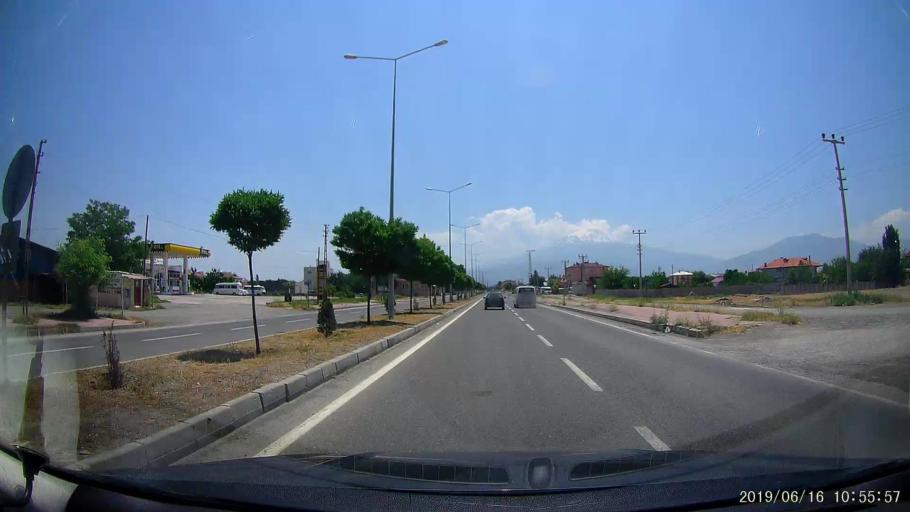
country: TR
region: Igdir
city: Igdir
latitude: 39.9333
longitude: 44.0160
